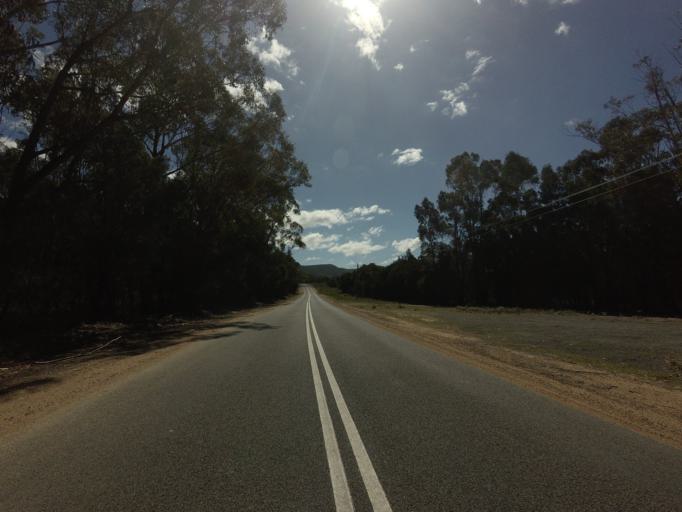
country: AU
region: Tasmania
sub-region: Break O'Day
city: St Helens
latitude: -41.6800
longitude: 148.2792
